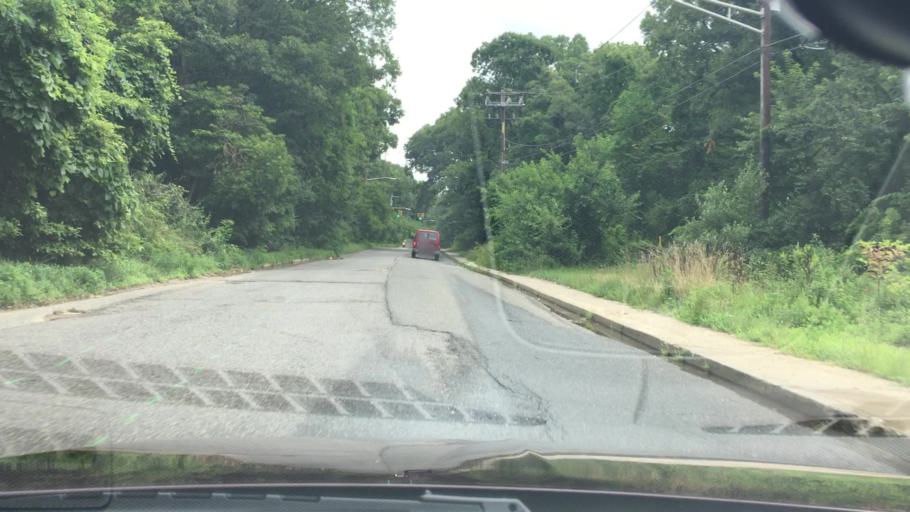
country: US
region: New York
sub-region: Suffolk County
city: Brentwood
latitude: 40.8226
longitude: -73.2508
